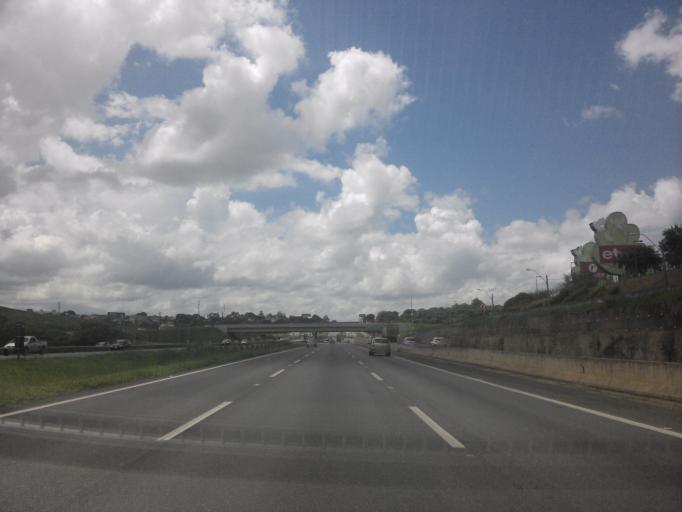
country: BR
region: Sao Paulo
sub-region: Campinas
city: Campinas
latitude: -22.8442
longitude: -47.0657
